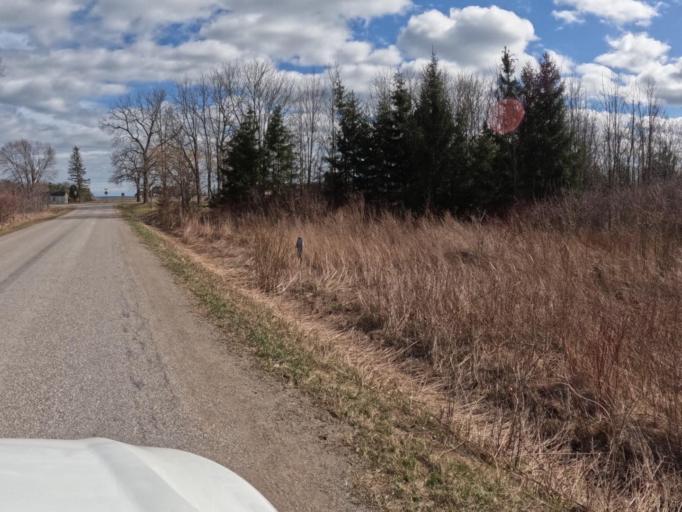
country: CA
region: Ontario
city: Norfolk County
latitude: 42.7507
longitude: -80.2742
